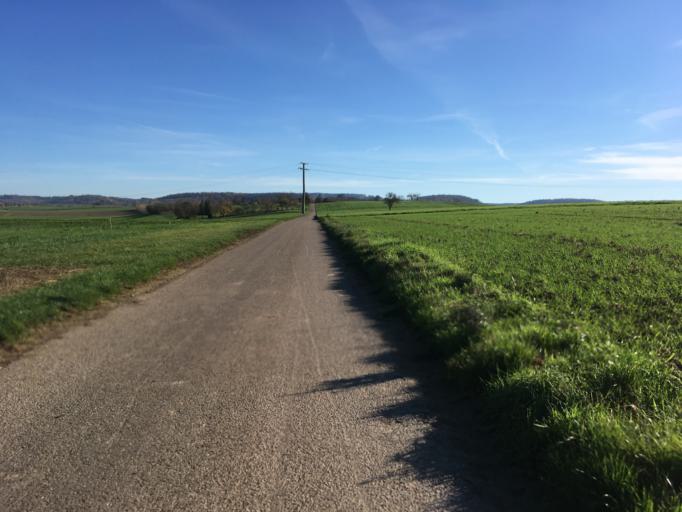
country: DE
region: Baden-Wuerttemberg
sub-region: Karlsruhe Region
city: Oberderdingen
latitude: 49.0766
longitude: 8.7985
